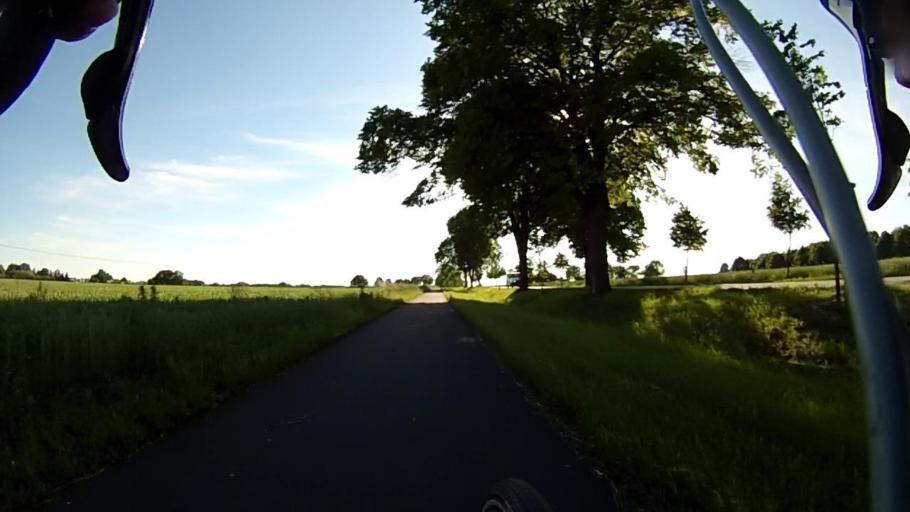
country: DE
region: Brandenburg
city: Ahrensfelde
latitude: 52.6102
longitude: 13.6449
